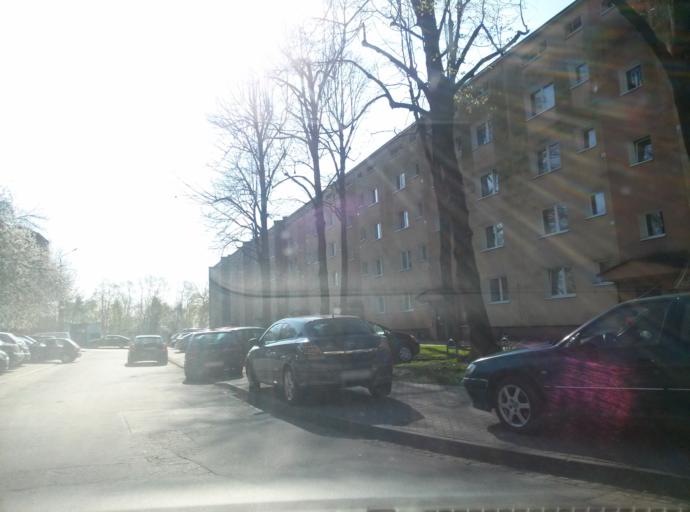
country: PL
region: Lesser Poland Voivodeship
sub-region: Powiat wielicki
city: Kokotow
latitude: 50.0947
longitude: 20.0617
